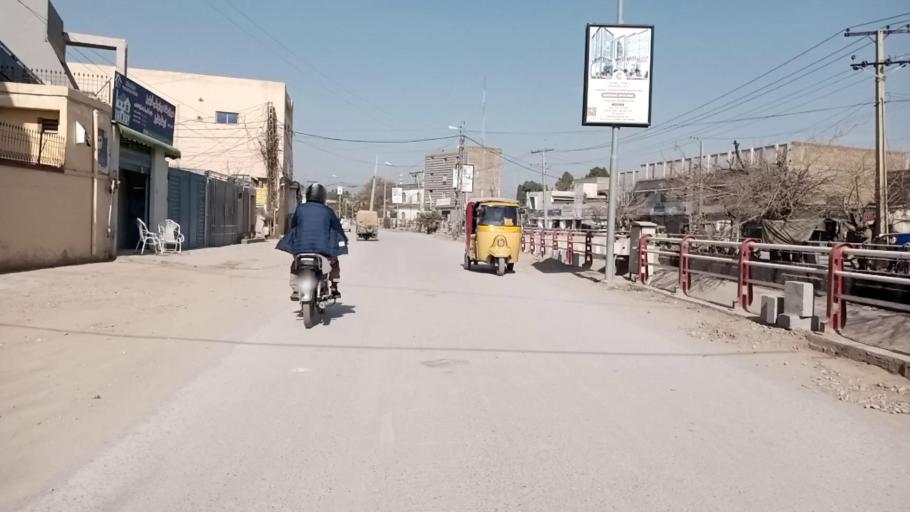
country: PK
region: Khyber Pakhtunkhwa
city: Peshawar
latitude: 33.9868
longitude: 71.4976
